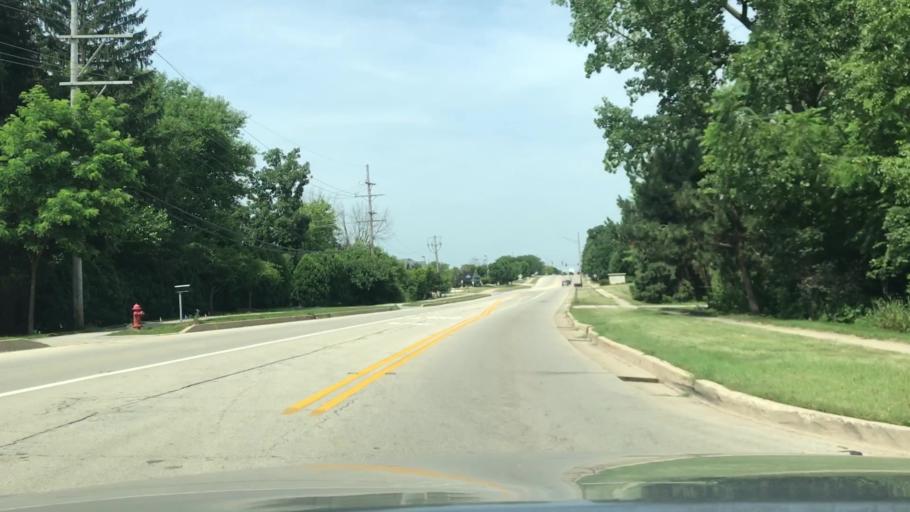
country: US
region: Illinois
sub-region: DuPage County
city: Darien
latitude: 41.7367
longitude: -88.0065
